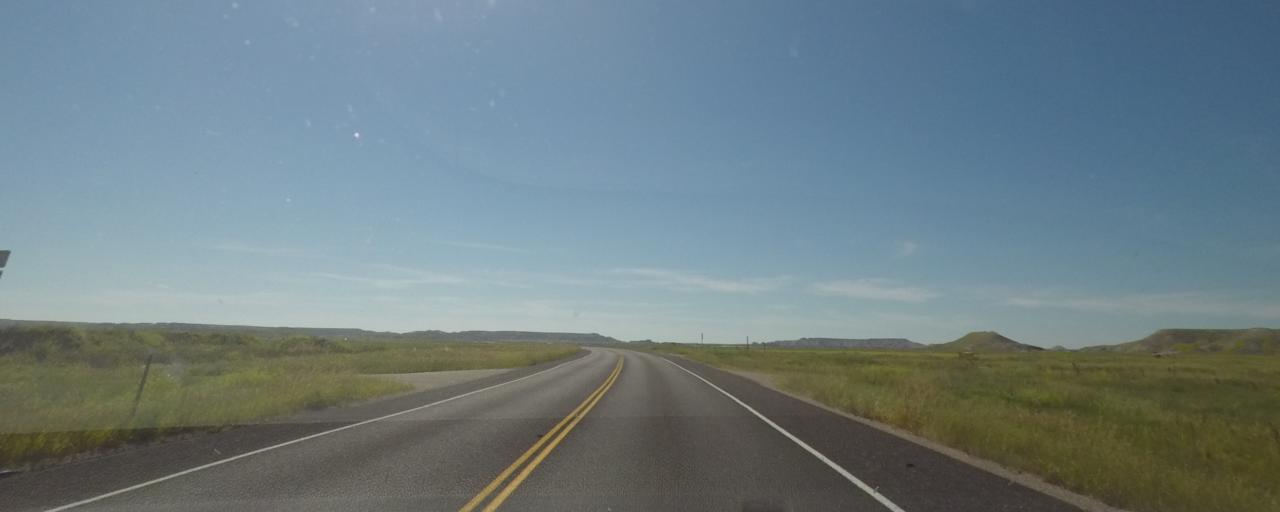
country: US
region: South Dakota
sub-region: Shannon County
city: Porcupine
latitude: 43.7810
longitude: -102.5511
